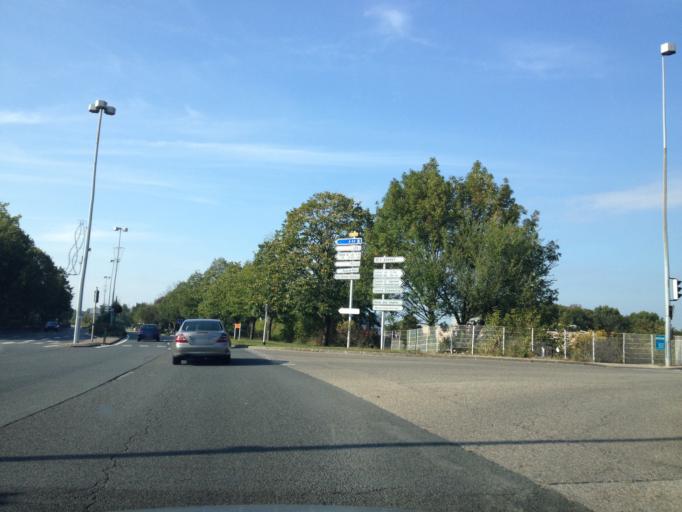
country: FR
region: Rhone-Alpes
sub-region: Departement de l'Isere
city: Villefontaine
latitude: 45.6099
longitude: 5.1562
